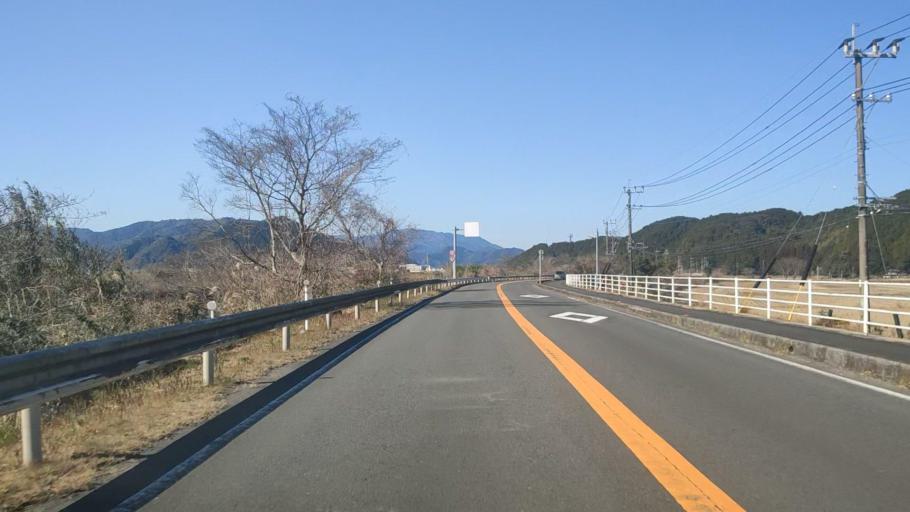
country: JP
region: Oita
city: Saiki
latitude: 32.9361
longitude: 131.9186
